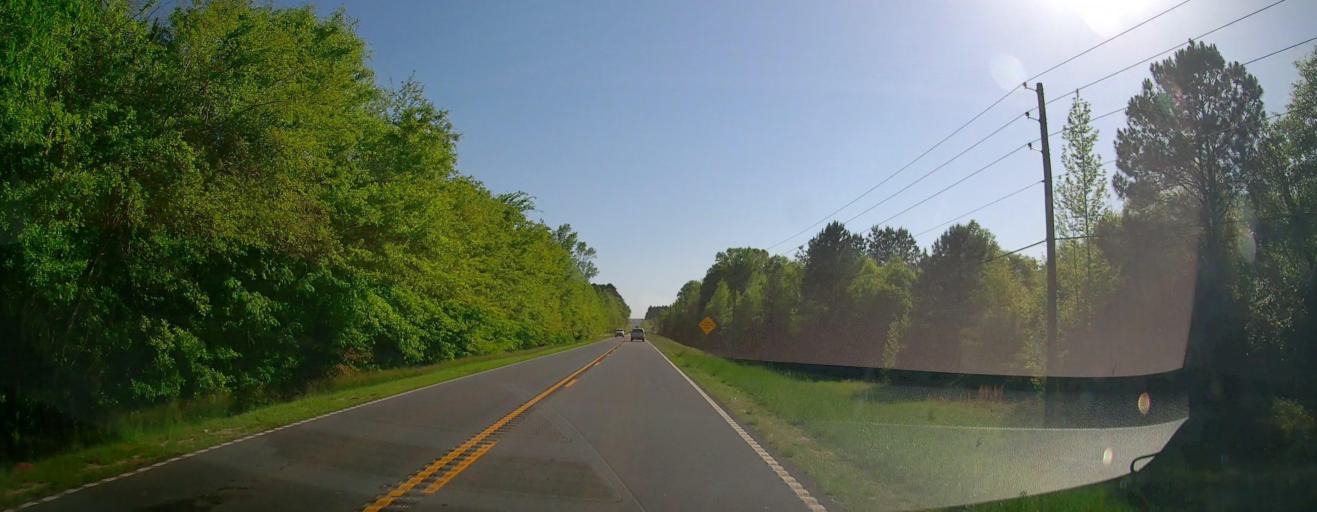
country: US
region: Georgia
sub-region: Houston County
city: Perry
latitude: 32.4534
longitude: -83.6217
